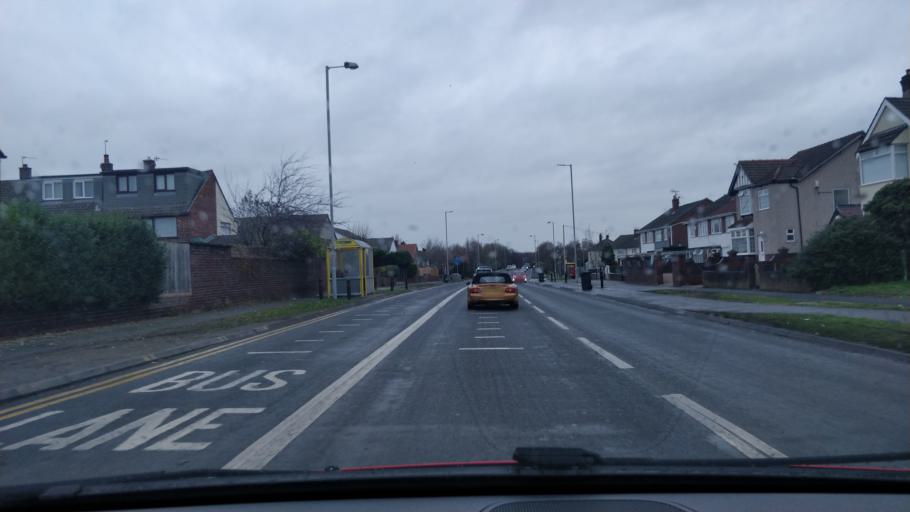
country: GB
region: England
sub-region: Sefton
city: Litherland
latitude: 53.4835
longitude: -2.9955
